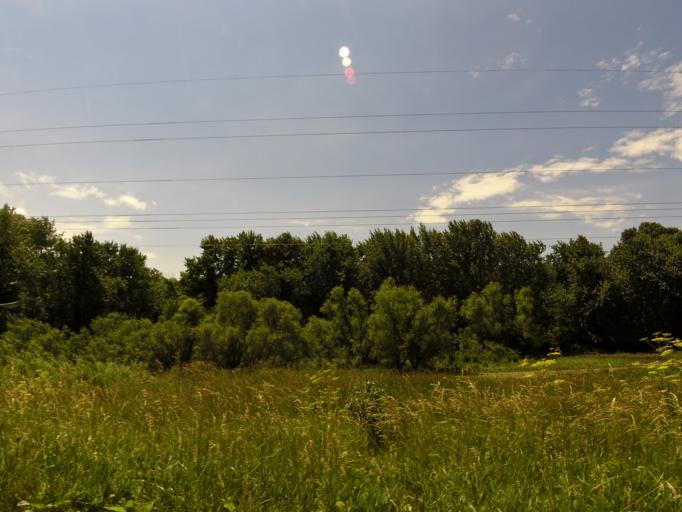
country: US
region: Iowa
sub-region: Bremer County
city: Tripoli
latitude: 42.7147
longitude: -92.1676
